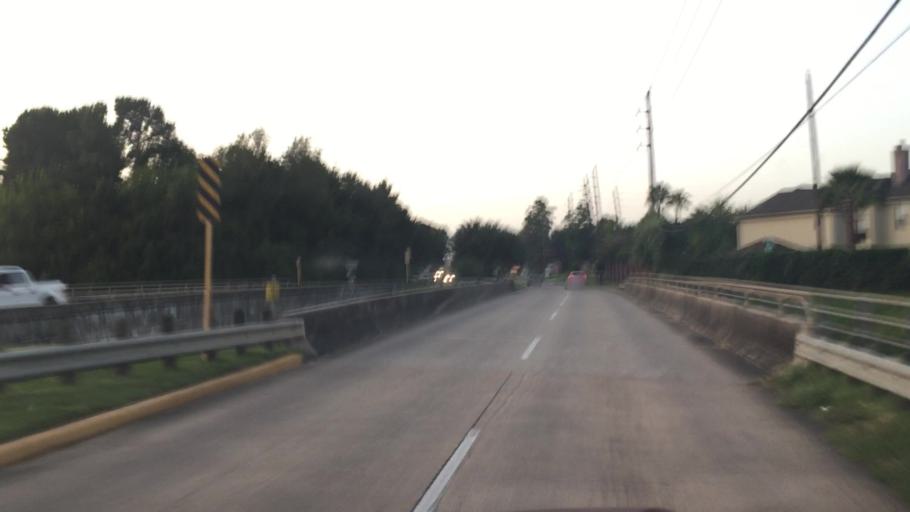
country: US
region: Texas
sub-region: Harris County
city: Tomball
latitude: 30.0285
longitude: -95.5316
